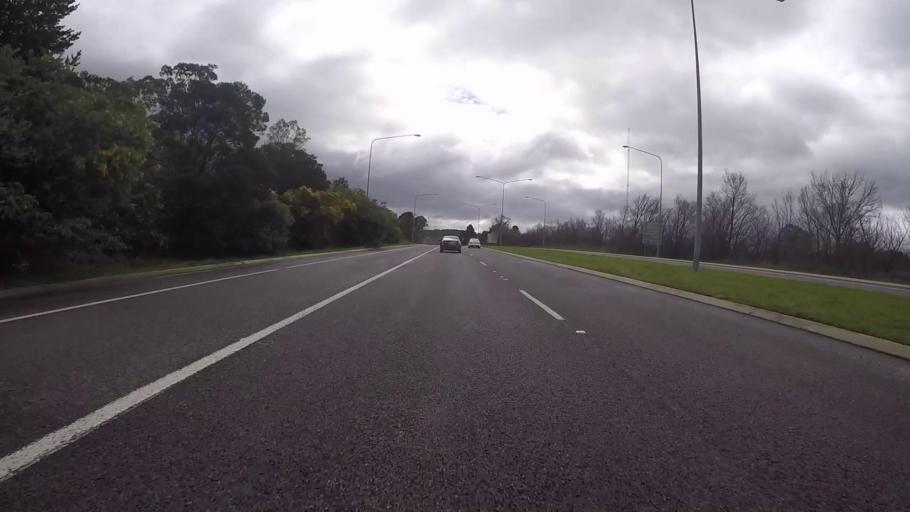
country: AU
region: Australian Capital Territory
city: Kaleen
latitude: -35.2226
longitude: 149.1208
